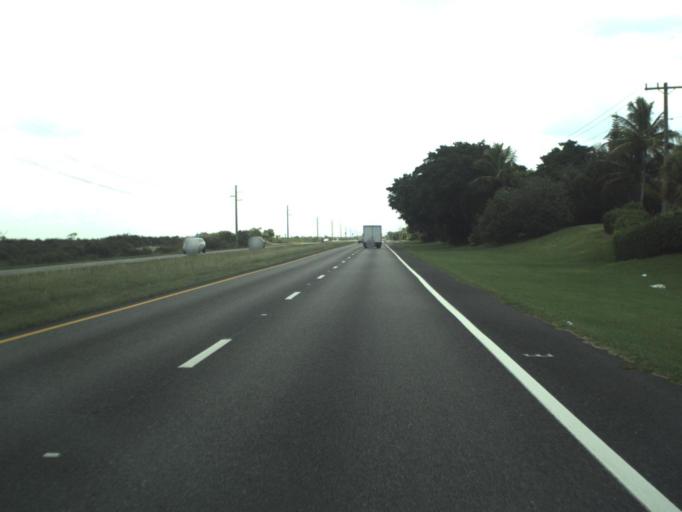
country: US
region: Florida
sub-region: Palm Beach County
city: Tequesta
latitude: 26.9931
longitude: -80.0955
